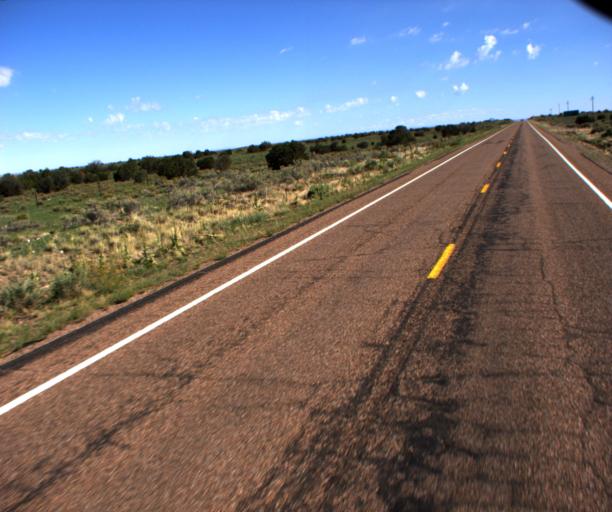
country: US
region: Arizona
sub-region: Coconino County
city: Williams
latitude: 35.5318
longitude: -112.1658
